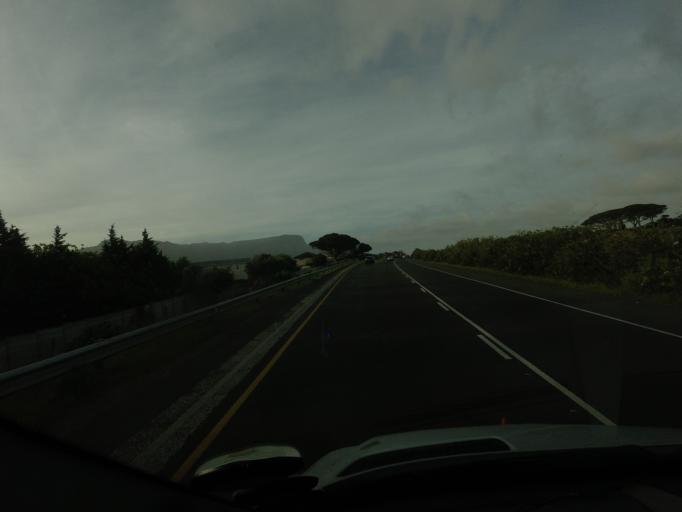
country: ZA
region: Western Cape
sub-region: City of Cape Town
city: Bergvliet
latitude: -34.0358
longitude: 18.4437
